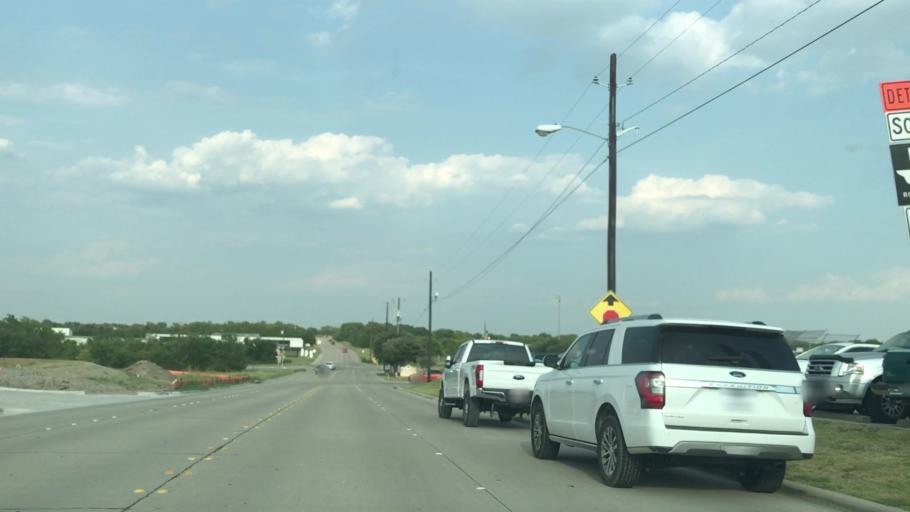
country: US
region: Texas
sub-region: Rockwall County
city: Rockwall
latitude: 32.9260
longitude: -96.4389
